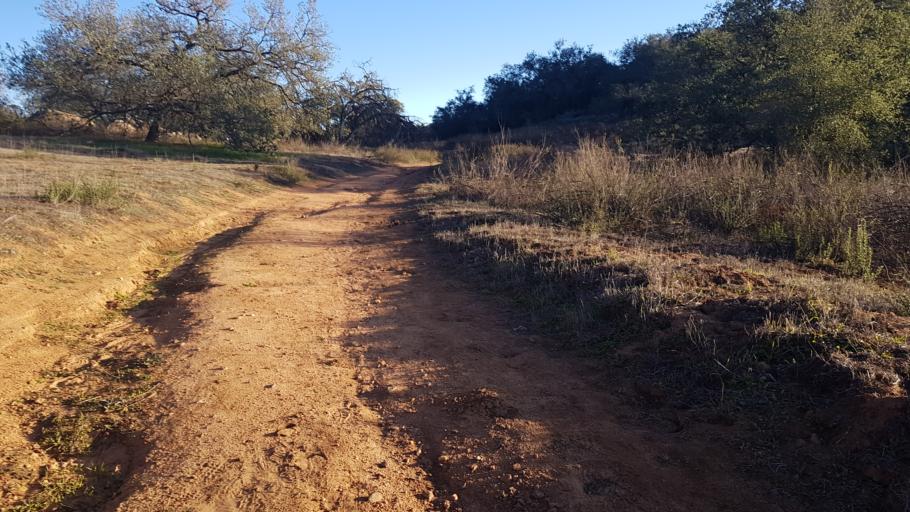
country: US
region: California
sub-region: San Diego County
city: Valley Center
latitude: 33.2079
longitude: -117.0648
